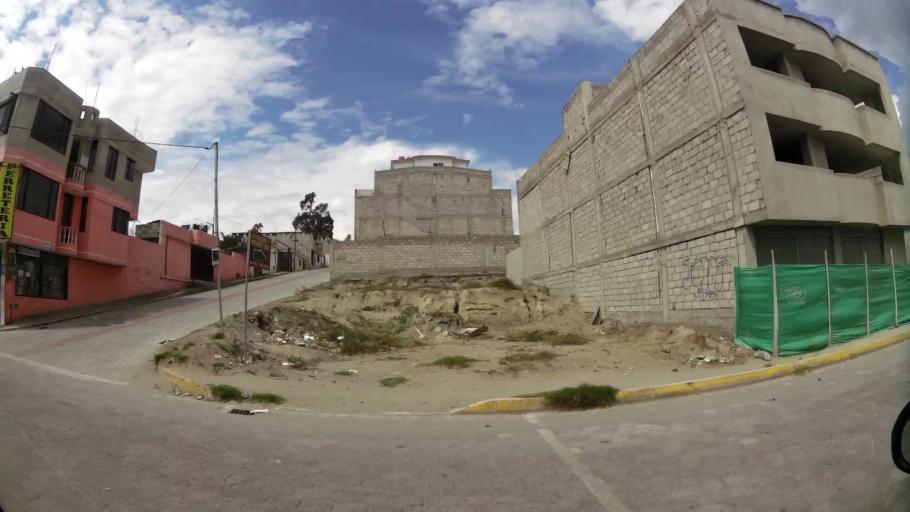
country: EC
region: Pichincha
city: Quito
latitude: -0.0703
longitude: -78.4338
